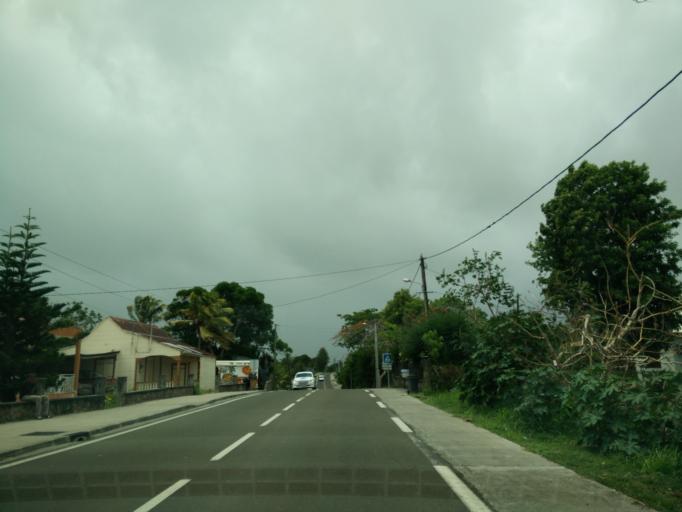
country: GP
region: Guadeloupe
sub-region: Guadeloupe
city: Grand-Bourg
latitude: 15.9029
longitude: -61.2521
